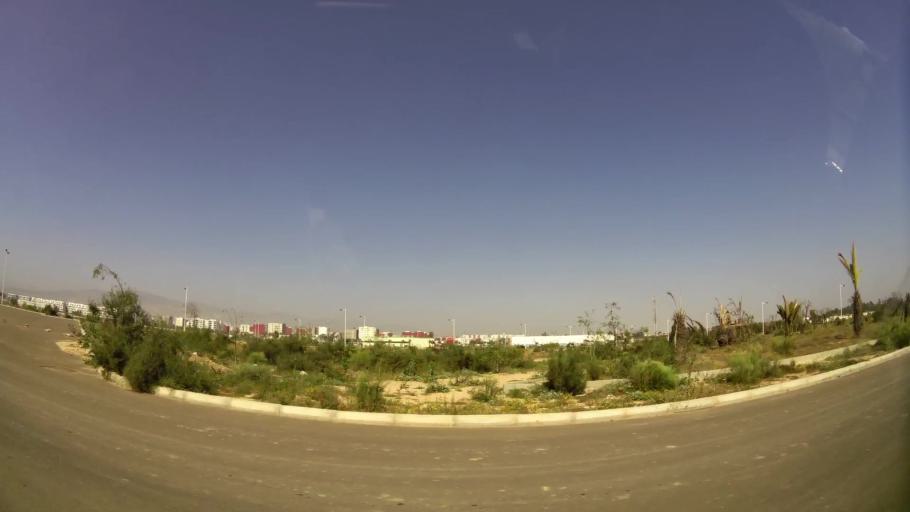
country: MA
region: Souss-Massa-Draa
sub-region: Agadir-Ida-ou-Tnan
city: Agadir
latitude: 30.3927
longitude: -9.5858
